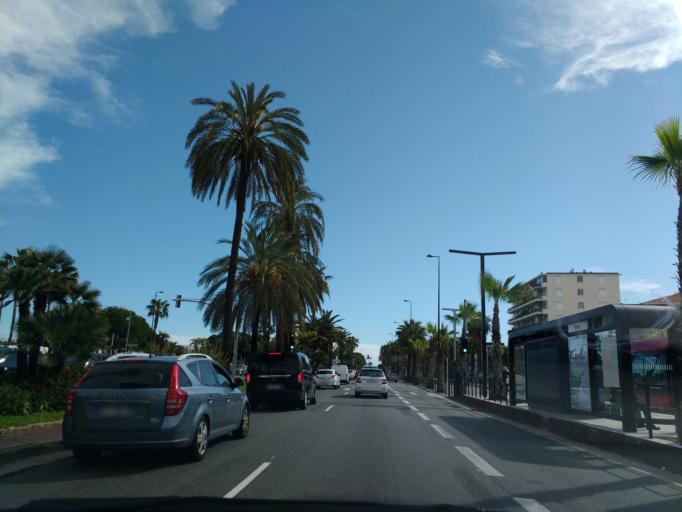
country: FR
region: Provence-Alpes-Cote d'Azur
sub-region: Departement des Alpes-Maritimes
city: Nice
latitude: 43.6769
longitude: 7.2285
